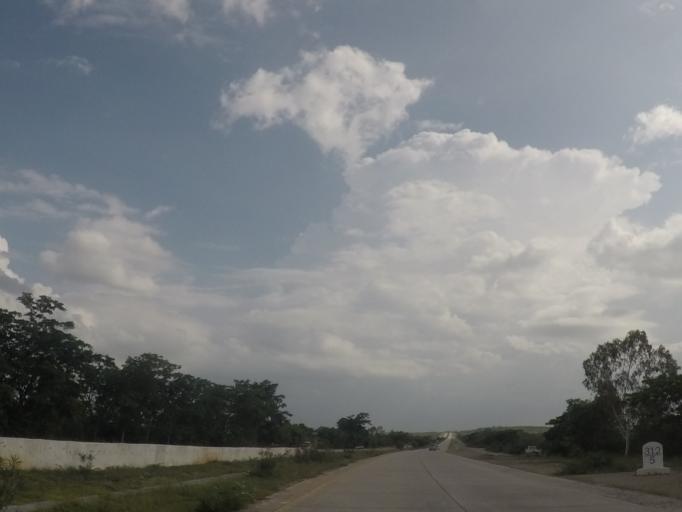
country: MM
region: Mandalay
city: Meiktila
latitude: 21.2088
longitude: 95.8329
